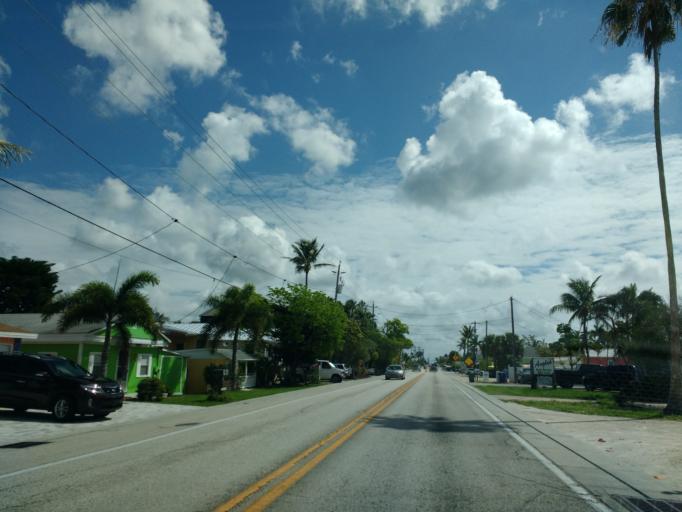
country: US
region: Florida
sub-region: Lee County
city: Pine Island Center
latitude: 26.6274
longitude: -82.0726
